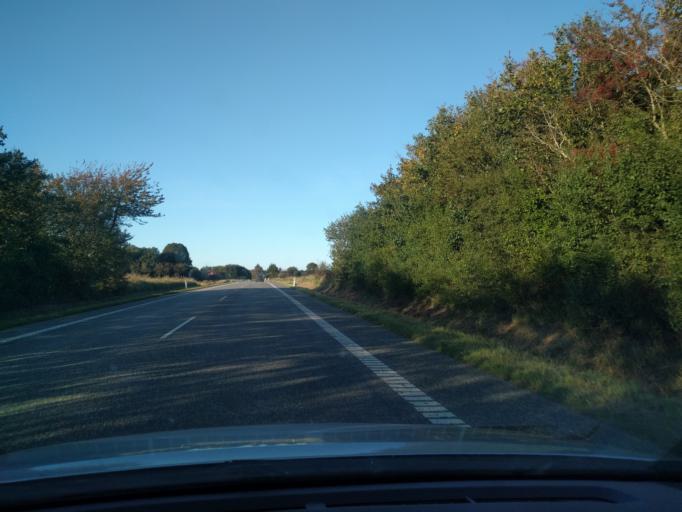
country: DK
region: Central Jutland
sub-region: Skanderborg Kommune
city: Ry
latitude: 56.1329
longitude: 9.7955
